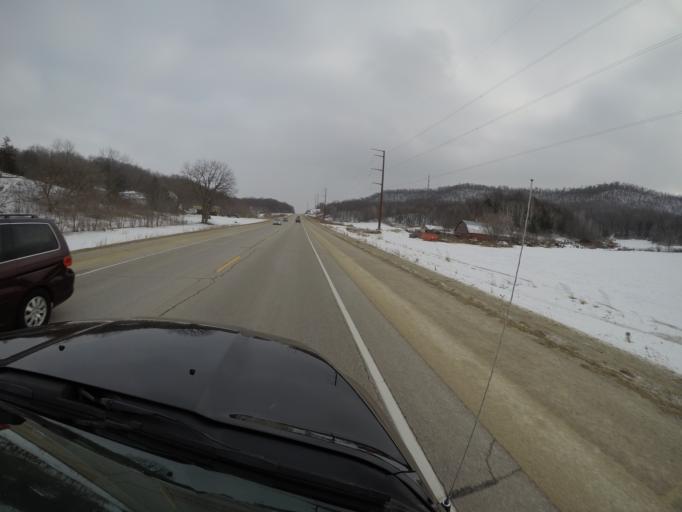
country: US
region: Wisconsin
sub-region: Trempealeau County
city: Galesville
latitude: 44.0740
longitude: -91.3349
